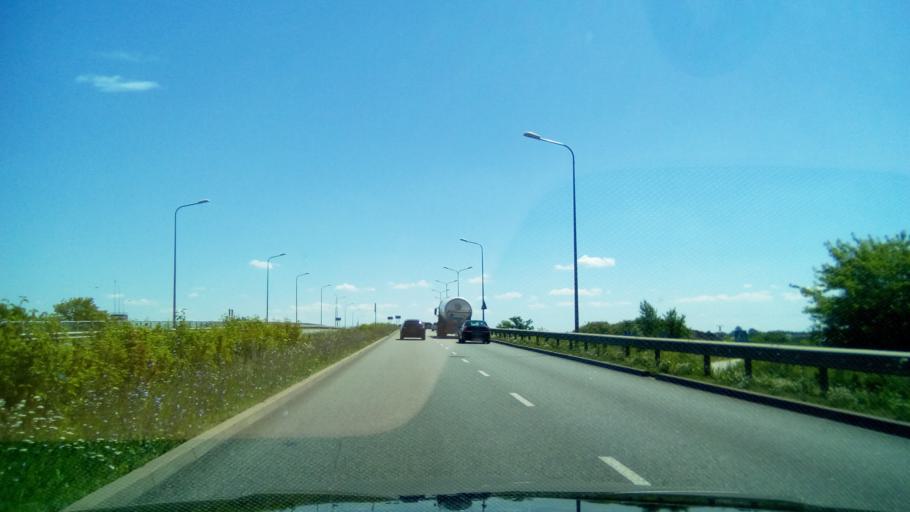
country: PL
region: Masovian Voivodeship
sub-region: Radom
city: Radom
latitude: 51.4203
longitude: 21.1830
